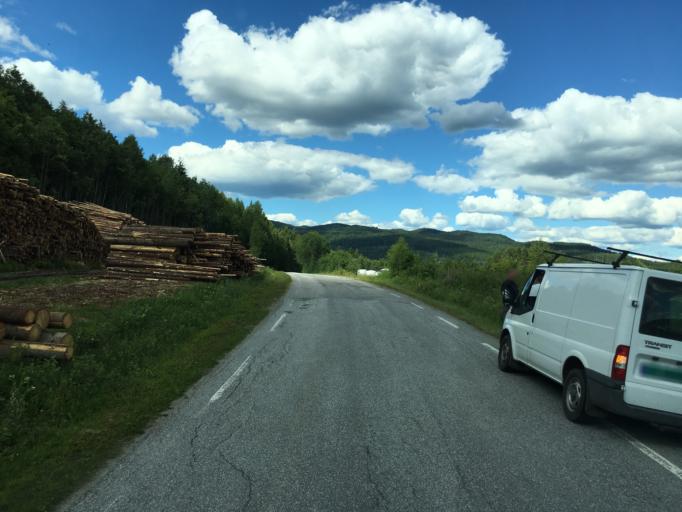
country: NO
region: Oppland
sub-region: Sondre Land
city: Hov
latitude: 60.5839
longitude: 10.2968
